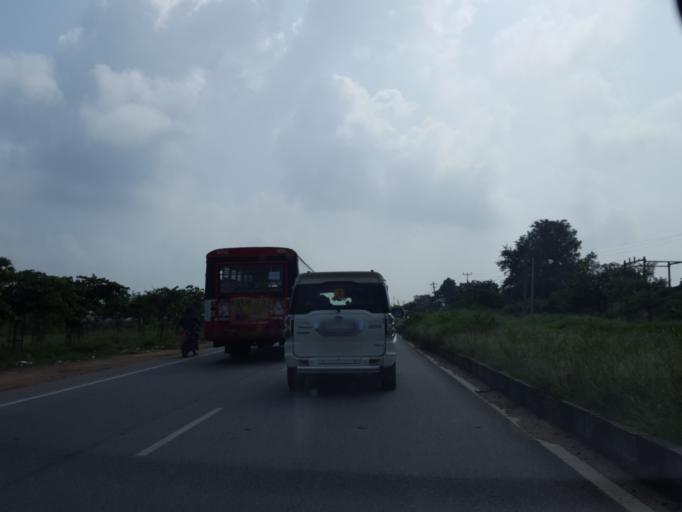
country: IN
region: Telangana
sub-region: Rangareddi
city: Ghatkesar
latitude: 17.2944
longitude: 78.7432
